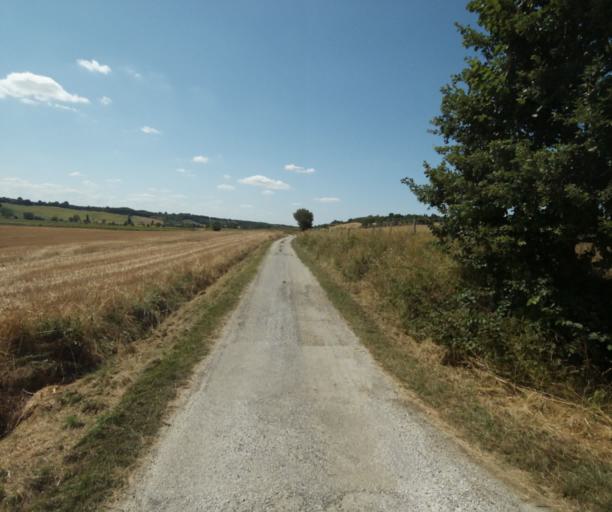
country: FR
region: Midi-Pyrenees
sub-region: Departement de la Haute-Garonne
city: Saint-Felix-Lauragais
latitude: 43.4941
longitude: 1.8827
